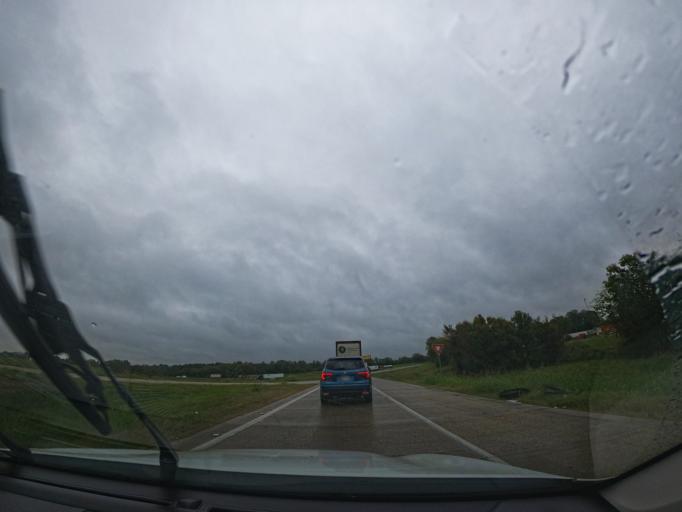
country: US
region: Louisiana
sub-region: Caddo Parish
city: Greenwood
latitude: 32.4452
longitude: -93.9806
